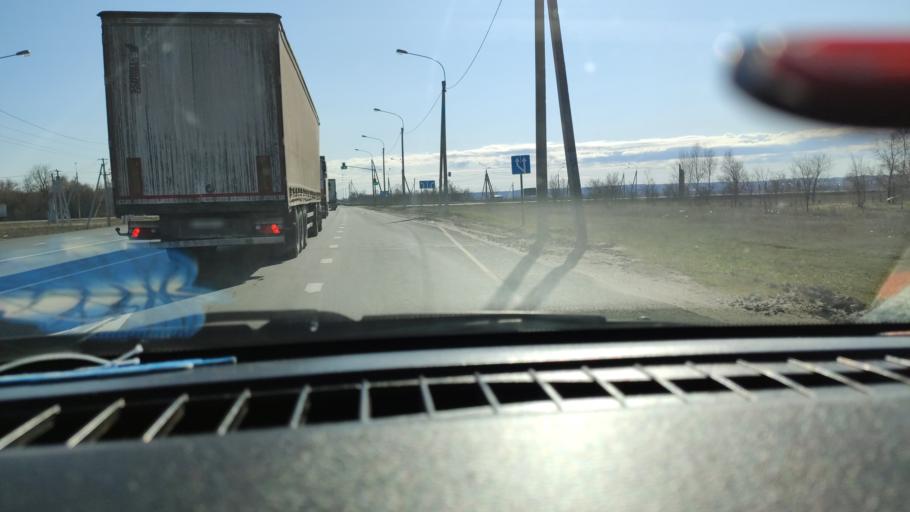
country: RU
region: Samara
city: Syzran'
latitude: 53.2087
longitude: 48.5074
